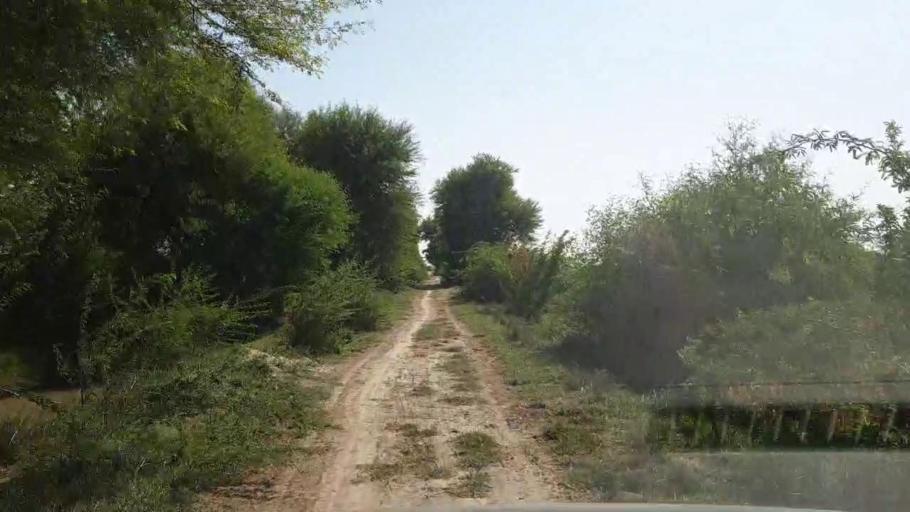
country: PK
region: Sindh
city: Kadhan
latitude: 24.6266
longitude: 68.9942
